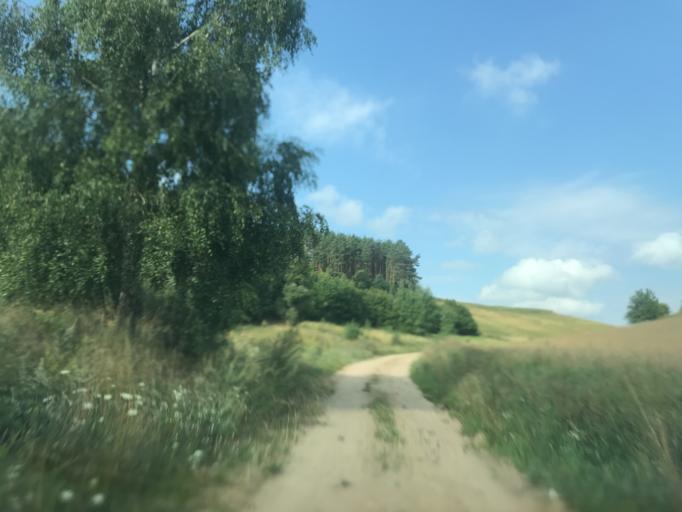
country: PL
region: Warmian-Masurian Voivodeship
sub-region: Powiat nowomiejski
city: Kurzetnik
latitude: 53.3496
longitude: 19.5077
